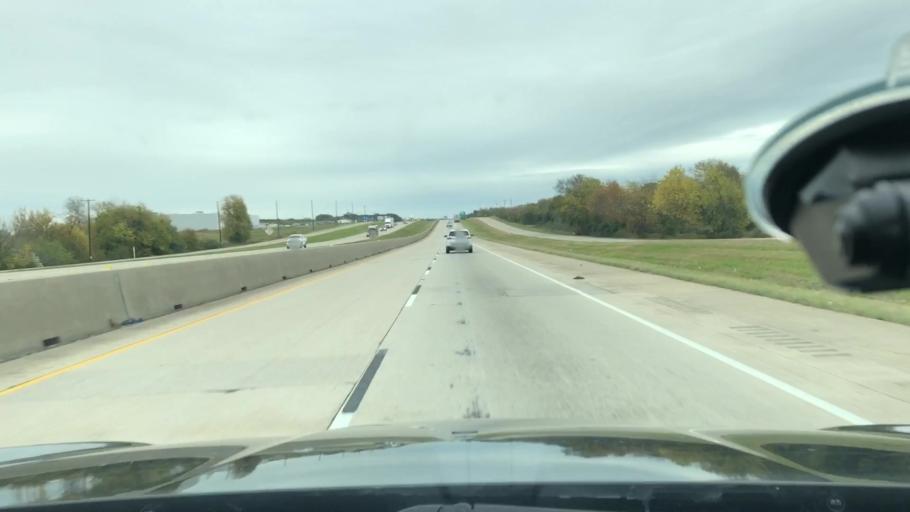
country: US
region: Texas
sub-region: Hopkins County
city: Sulphur Springs
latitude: 33.1209
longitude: -95.6626
